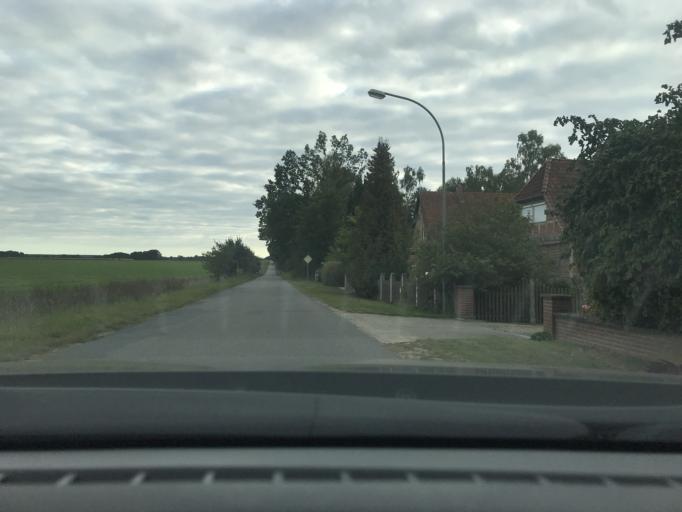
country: DE
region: Lower Saxony
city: Suderburg
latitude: 52.9146
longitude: 10.4580
